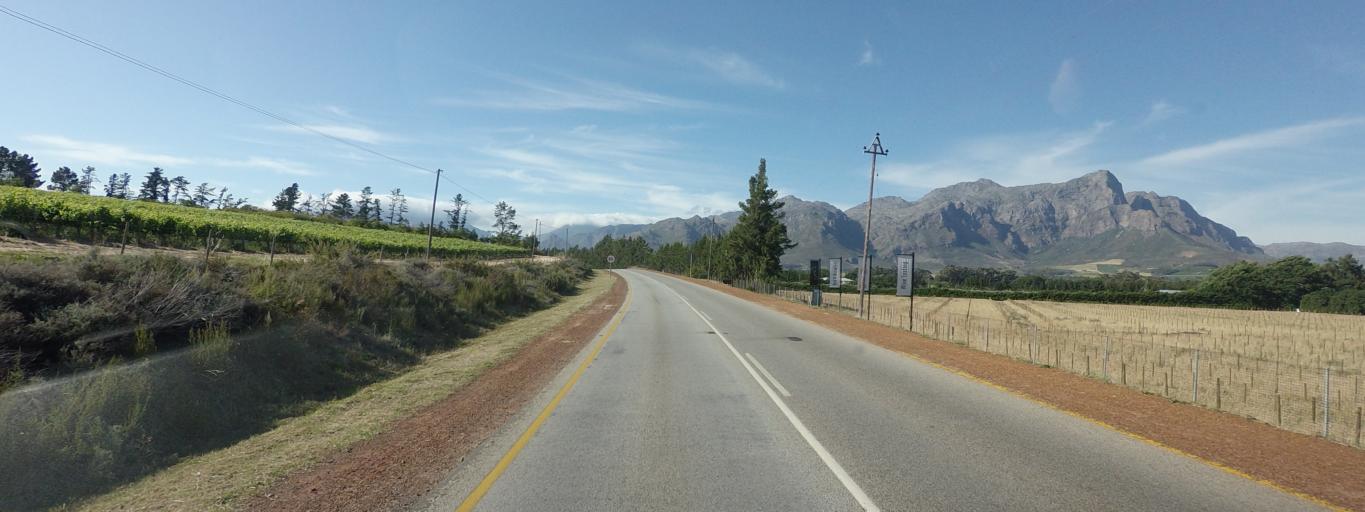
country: ZA
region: Western Cape
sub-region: Cape Winelands District Municipality
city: Paarl
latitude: -33.8618
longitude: 19.0394
